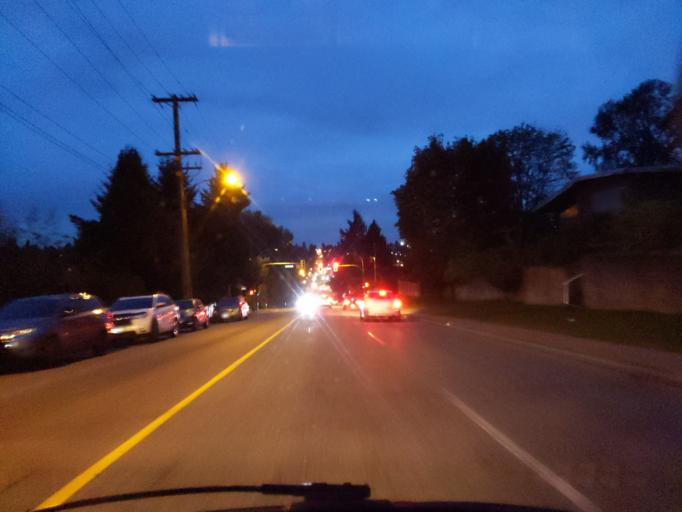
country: CA
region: British Columbia
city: New Westminster
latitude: 49.2248
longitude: -122.9075
